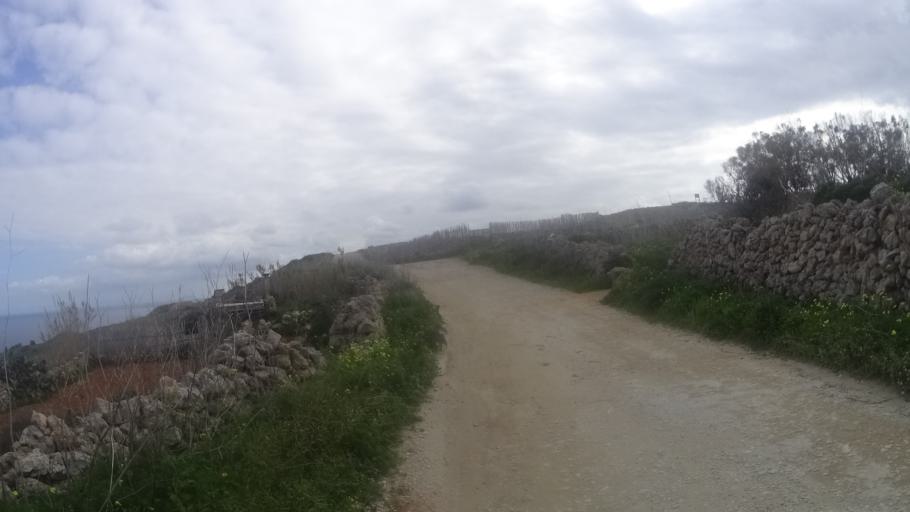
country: MT
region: Il-Qala
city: Qala
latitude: 36.0399
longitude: 14.3221
